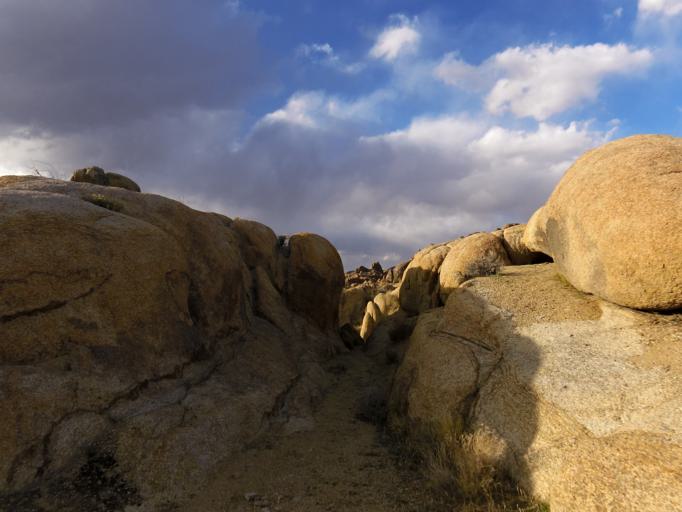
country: US
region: California
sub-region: Inyo County
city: Lone Pine
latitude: 36.6009
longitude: -118.1173
